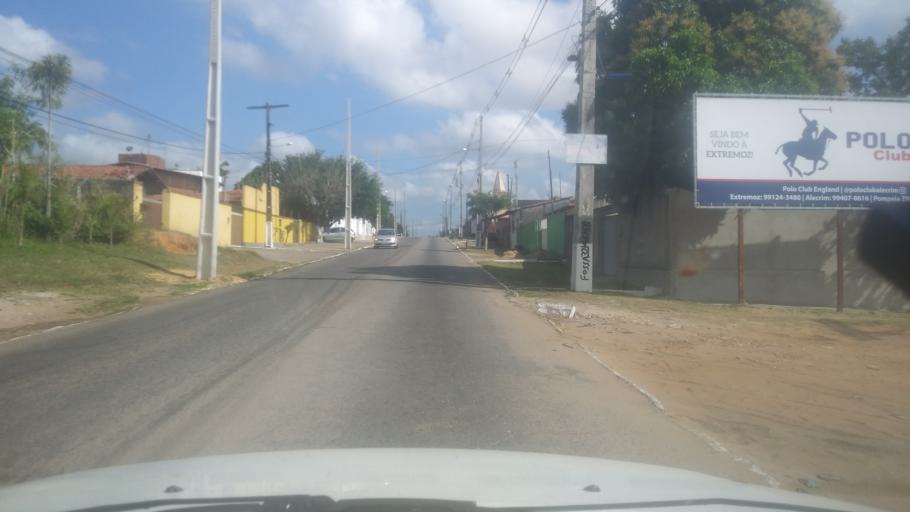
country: BR
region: Rio Grande do Norte
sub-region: Extremoz
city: Extremoz
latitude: -5.7090
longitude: -35.2787
